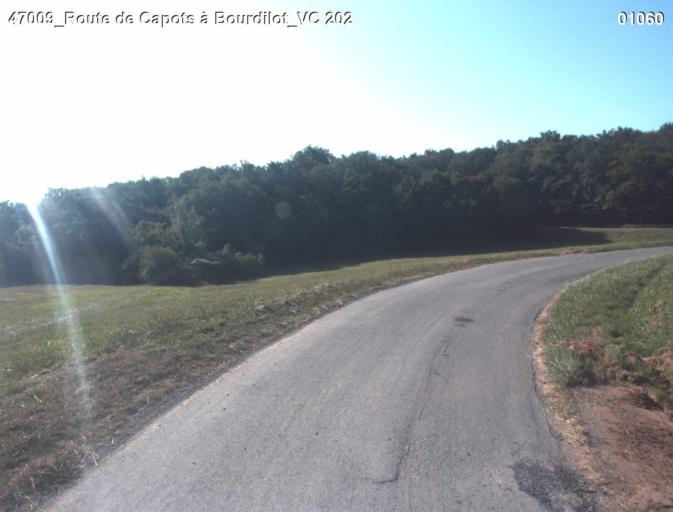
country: FR
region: Aquitaine
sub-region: Departement du Lot-et-Garonne
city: Mezin
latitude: 44.1021
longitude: 0.2981
